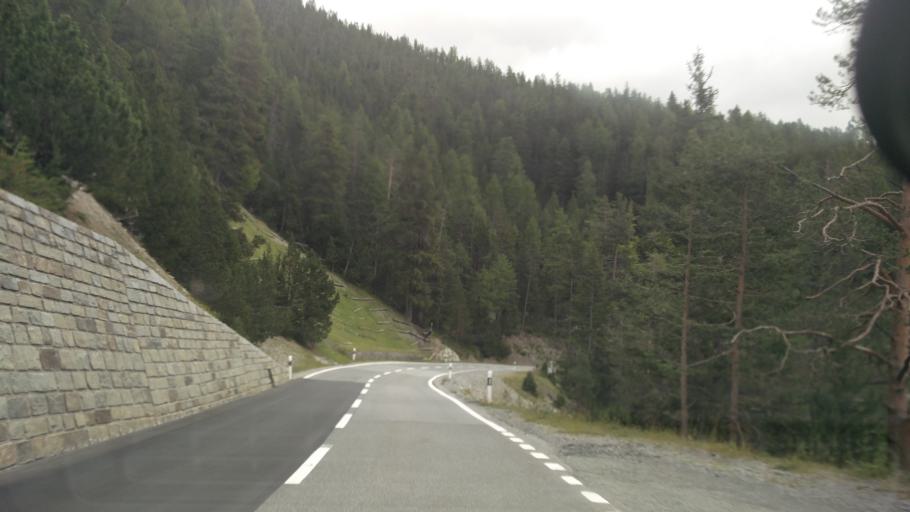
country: CH
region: Grisons
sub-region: Inn District
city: Zernez
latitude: 46.6735
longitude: 10.1677
